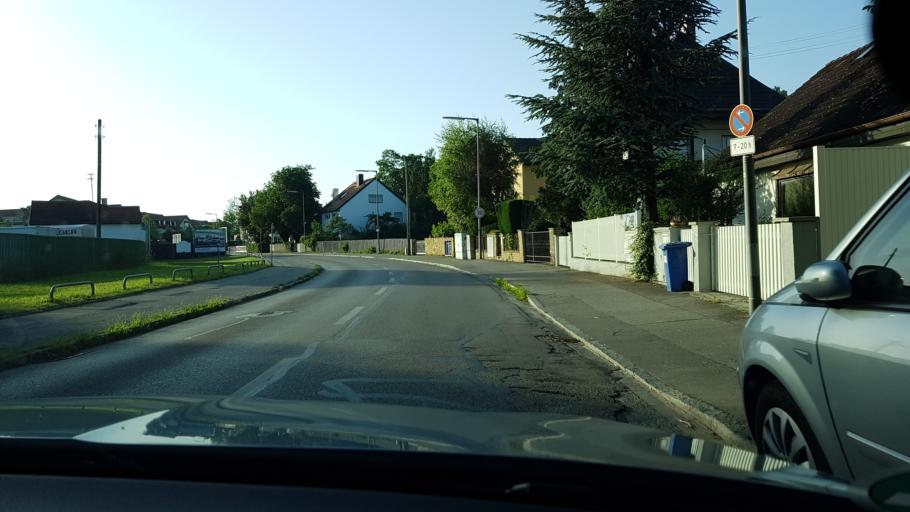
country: DE
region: Bavaria
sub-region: Upper Bavaria
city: Bogenhausen
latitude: 48.1441
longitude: 11.6607
